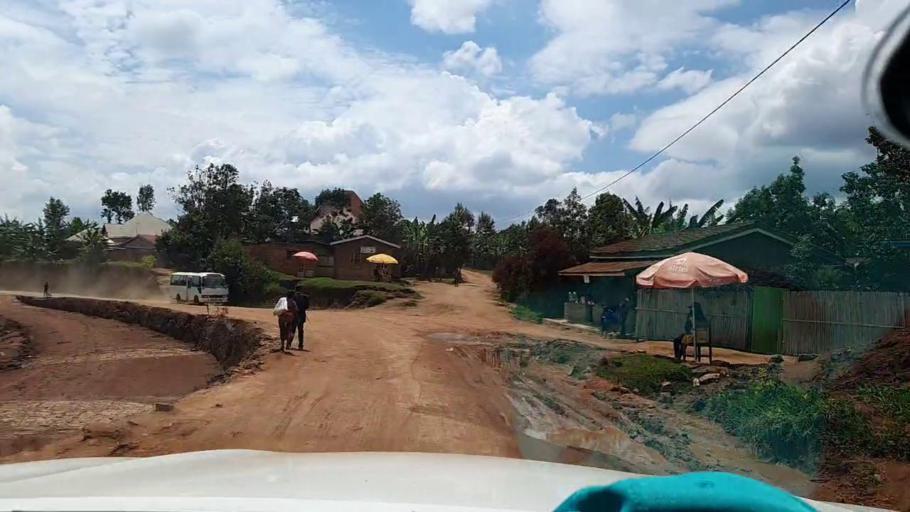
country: RW
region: Southern Province
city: Nzega
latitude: -2.6524
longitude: 29.5567
